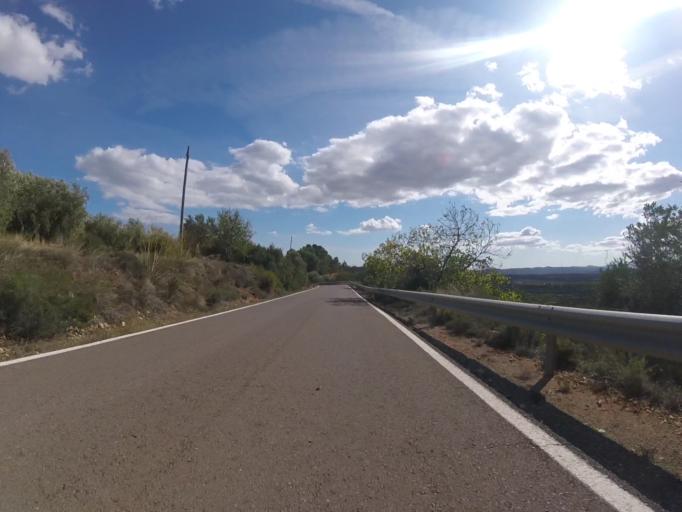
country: ES
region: Valencia
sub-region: Provincia de Castello
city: Cuevas de Vinroma
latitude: 40.3787
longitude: 0.1114
